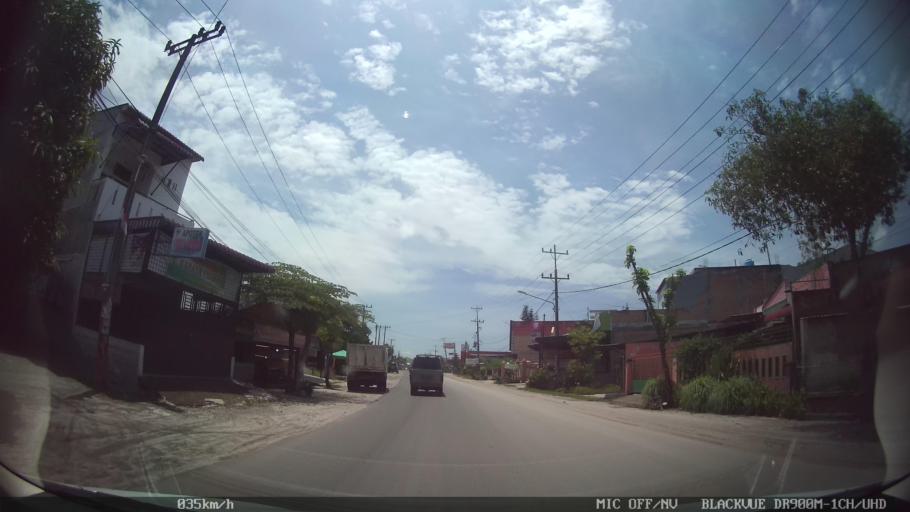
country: ID
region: North Sumatra
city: Perbaungan
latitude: 3.5463
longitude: 98.8798
